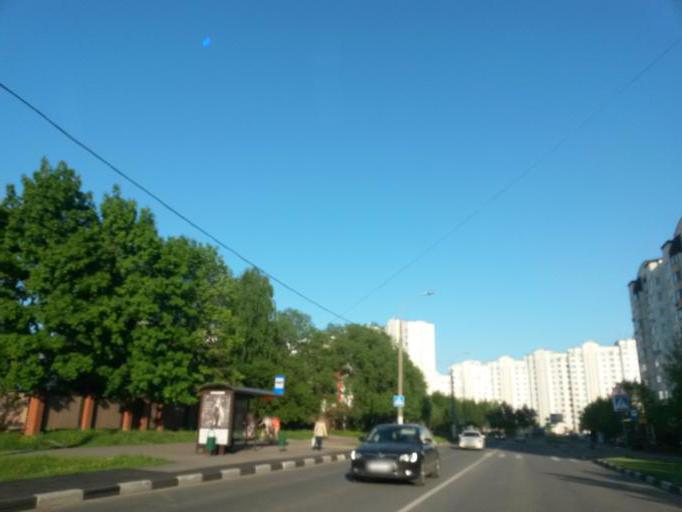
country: RU
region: Moscow
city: Annino
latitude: 55.5508
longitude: 37.5651
